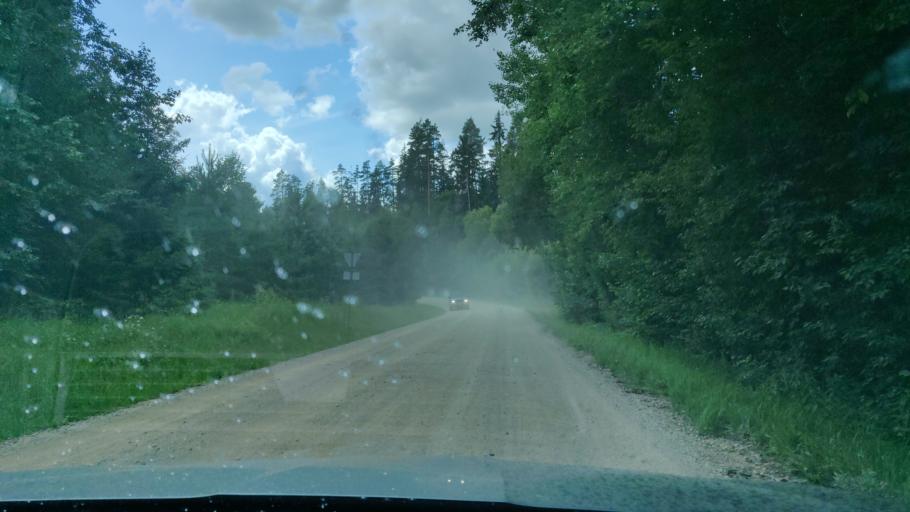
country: EE
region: Vorumaa
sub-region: Antsla vald
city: Vana-Antsla
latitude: 58.0211
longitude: 26.5795
